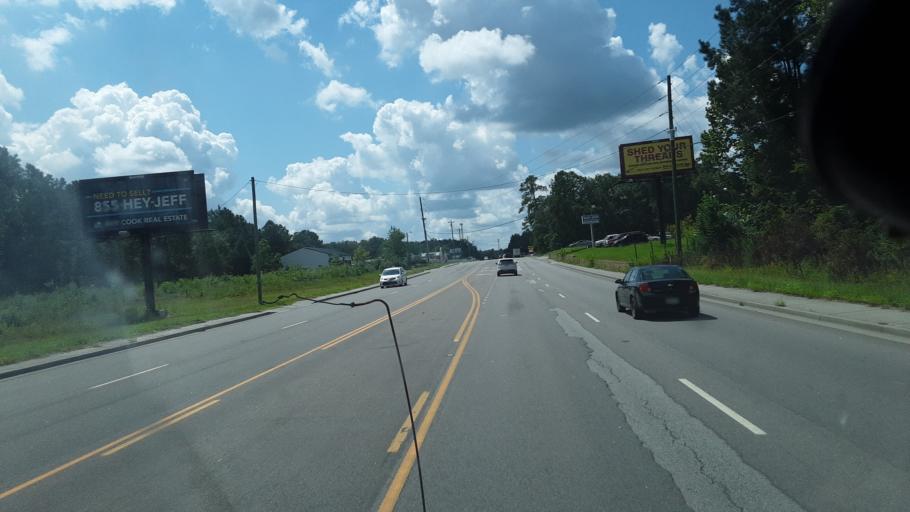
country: US
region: South Carolina
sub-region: Berkeley County
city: Sangaree
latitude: 33.0853
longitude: -80.0820
